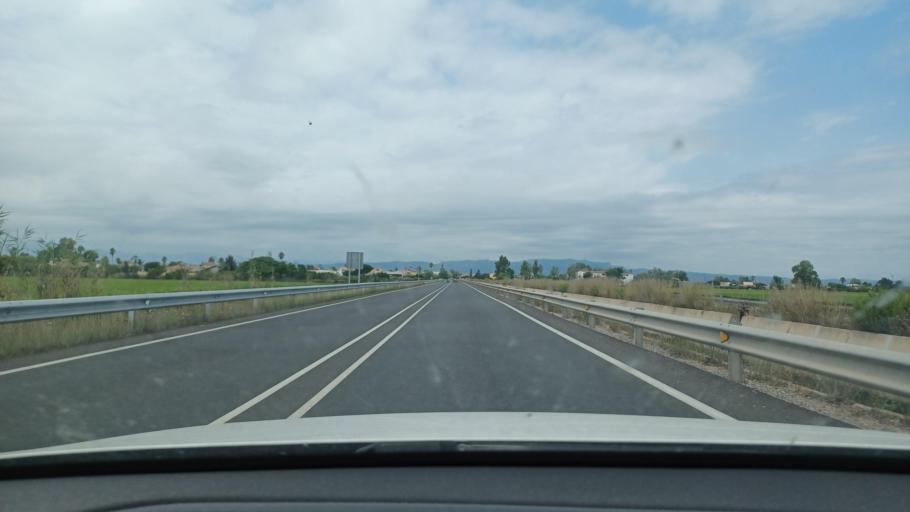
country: ES
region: Catalonia
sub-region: Provincia de Tarragona
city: Deltebre
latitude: 40.7138
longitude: 0.7544
